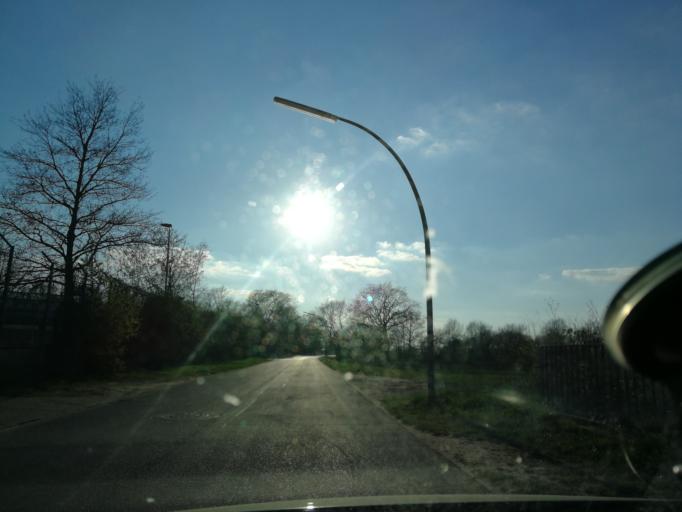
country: DE
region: Lower Saxony
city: Neu Wulmstorf
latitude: 53.4762
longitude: 9.8409
